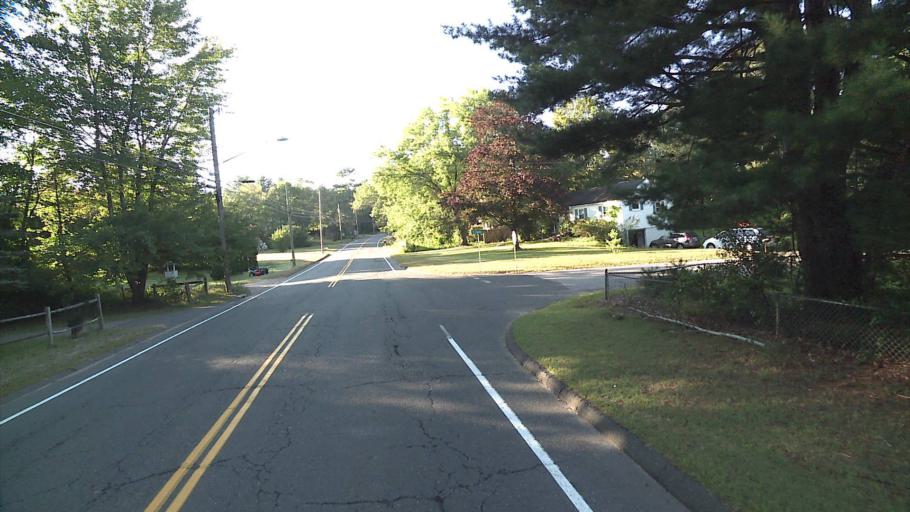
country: US
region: Connecticut
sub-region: Tolland County
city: Mansfield City
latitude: 41.7536
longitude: -72.2620
